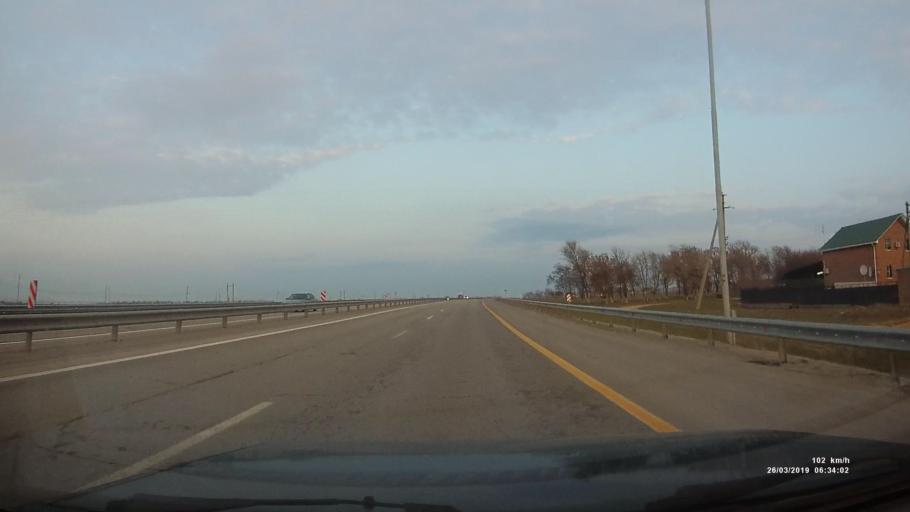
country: RU
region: Rostov
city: Chaltyr
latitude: 47.2751
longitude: 39.4751
